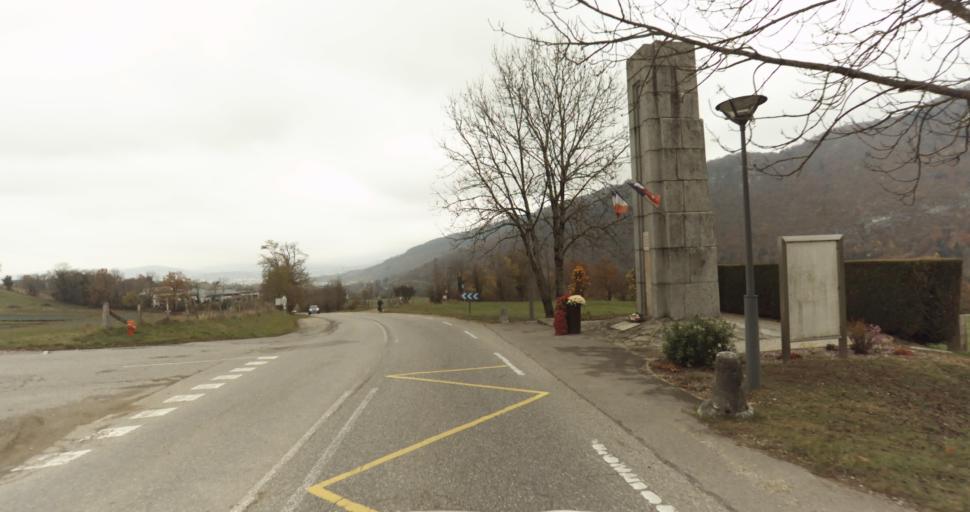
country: FR
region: Rhone-Alpes
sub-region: Departement de la Haute-Savoie
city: Seynod
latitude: 45.8668
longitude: 6.0945
